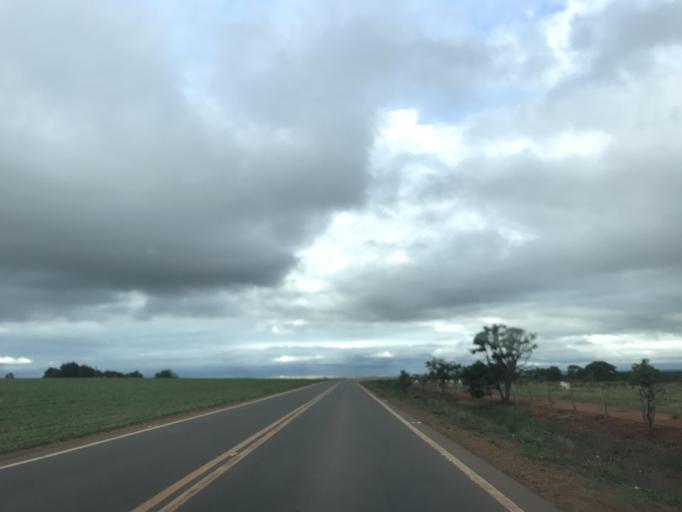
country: BR
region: Goias
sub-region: Luziania
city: Luziania
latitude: -16.3887
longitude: -48.1549
